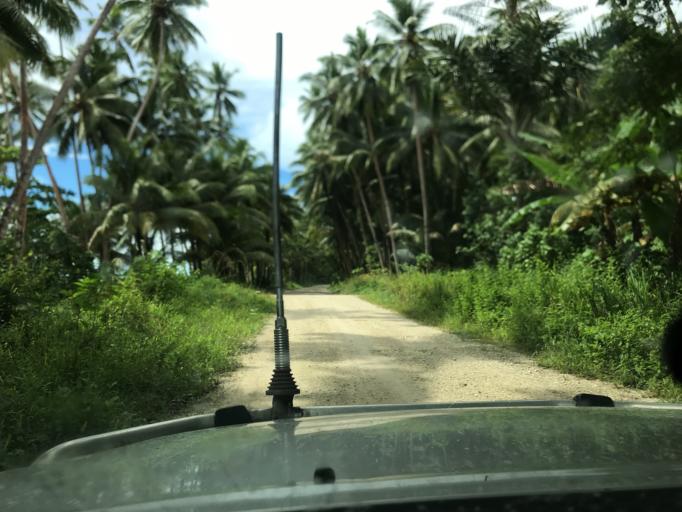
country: SB
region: Malaita
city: Auki
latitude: -8.3590
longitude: 160.6601
